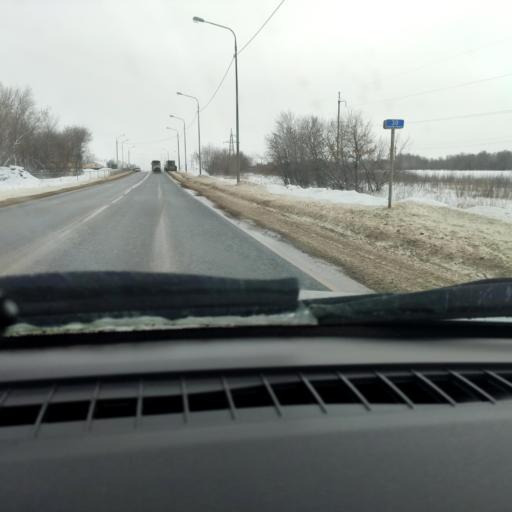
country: RU
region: Samara
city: Dubovyy Umet
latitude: 52.9760
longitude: 50.2736
